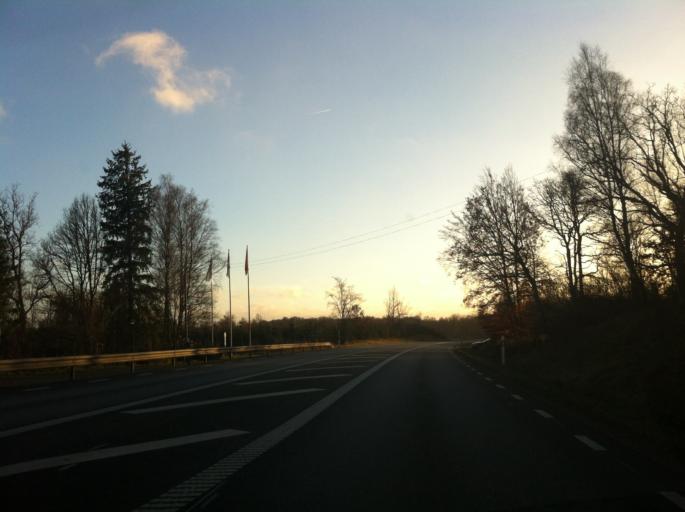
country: SE
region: Skane
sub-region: Hassleholms Kommun
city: Hassleholm
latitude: 56.1150
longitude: 13.7887
